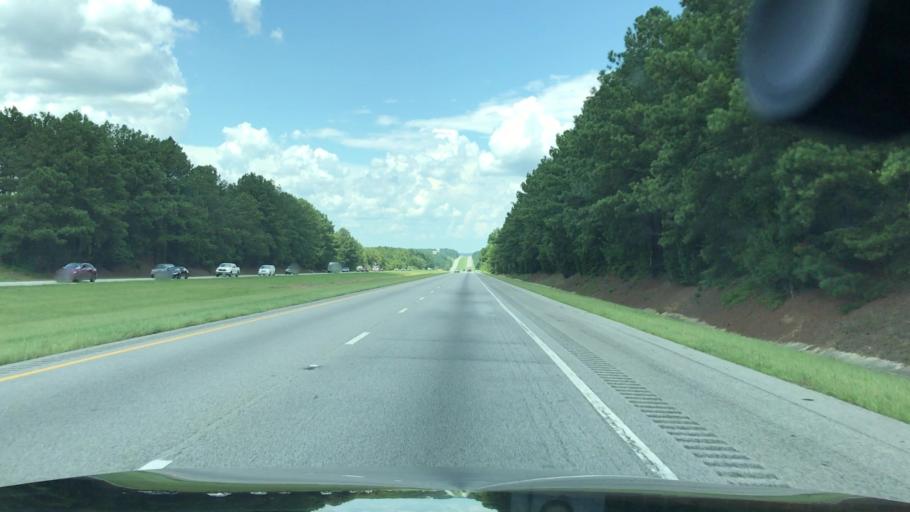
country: US
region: South Carolina
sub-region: Chester County
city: Great Falls
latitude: 34.5727
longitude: -81.0115
